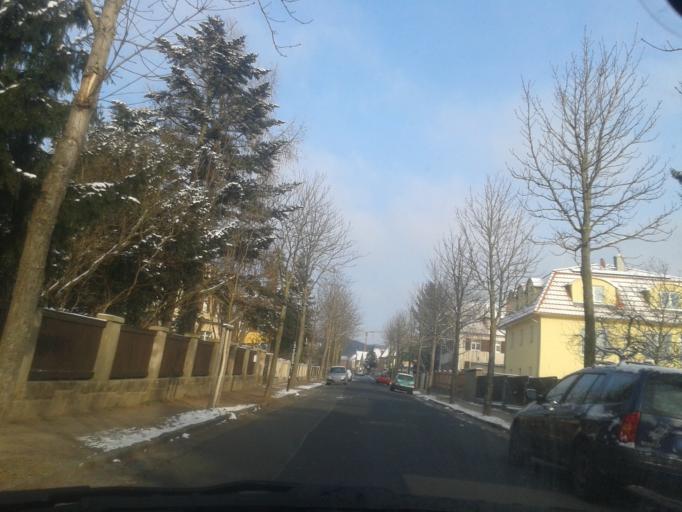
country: DE
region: Saxony
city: Radebeul
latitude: 51.1027
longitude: 13.6875
